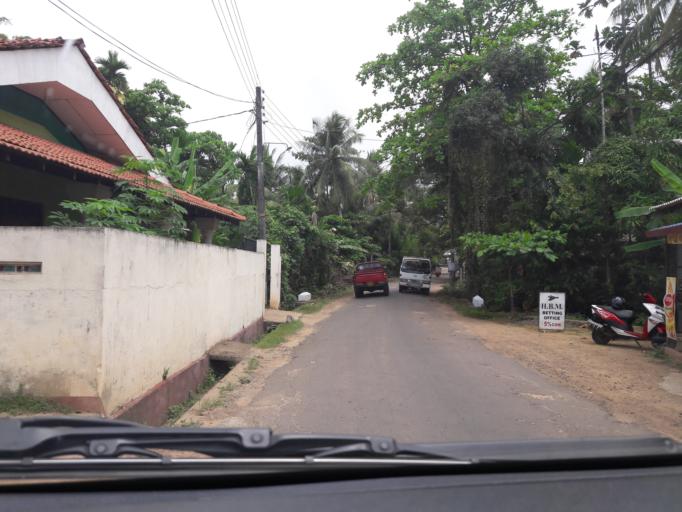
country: LK
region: Southern
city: Hikkaduwa
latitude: 6.1021
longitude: 80.1533
